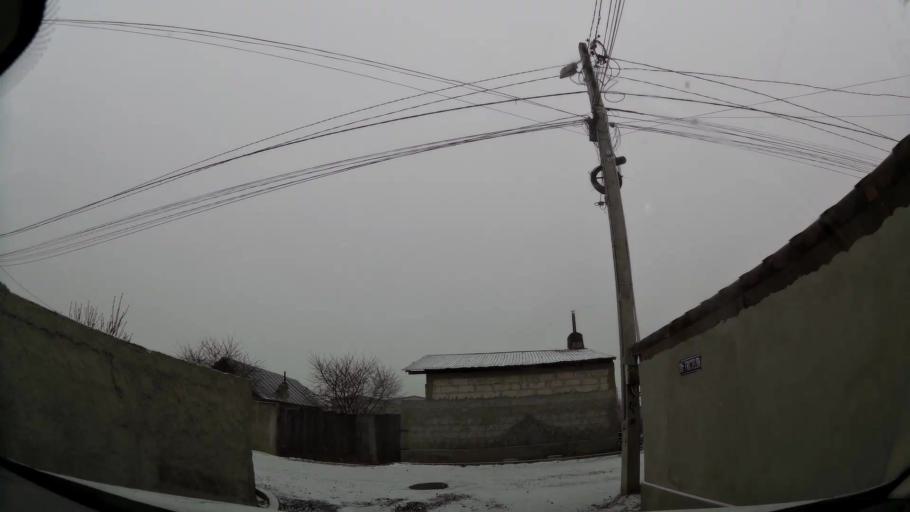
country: RO
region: Dambovita
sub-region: Comuna Ulmi
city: Ulmi
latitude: 44.9110
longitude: 25.4819
